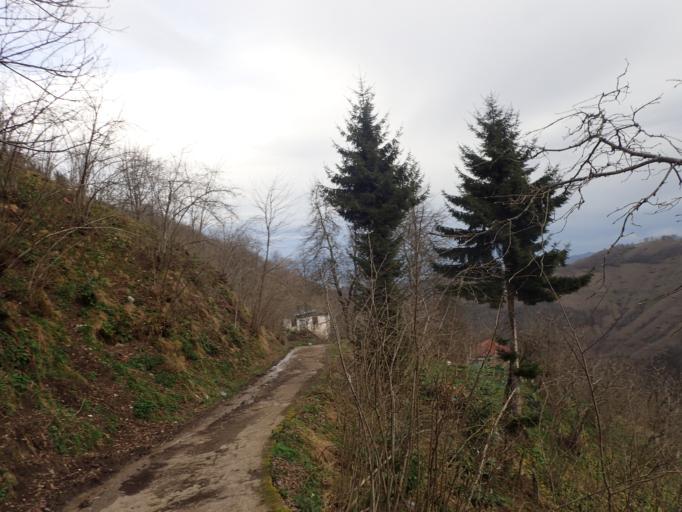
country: TR
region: Ordu
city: Camas
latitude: 40.8838
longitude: 37.5804
